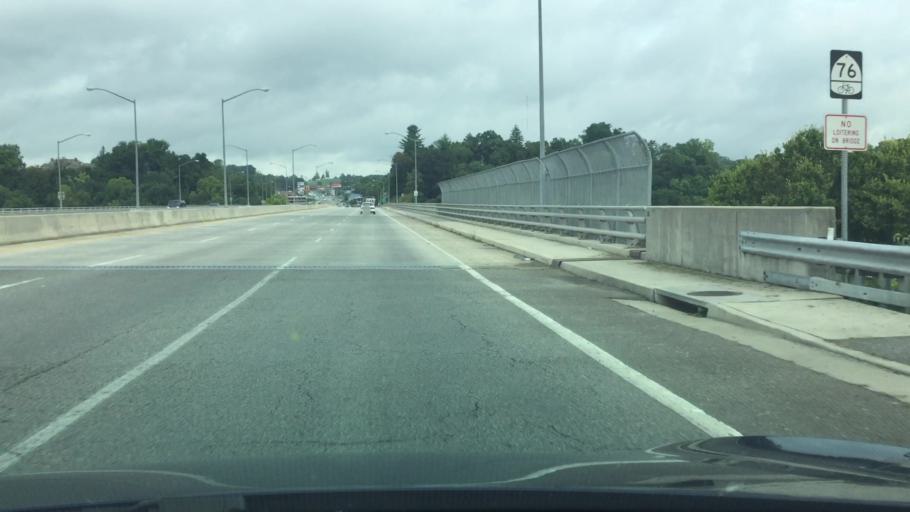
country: US
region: Virginia
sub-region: City of Radford
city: Radford
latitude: 37.1370
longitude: -80.5719
